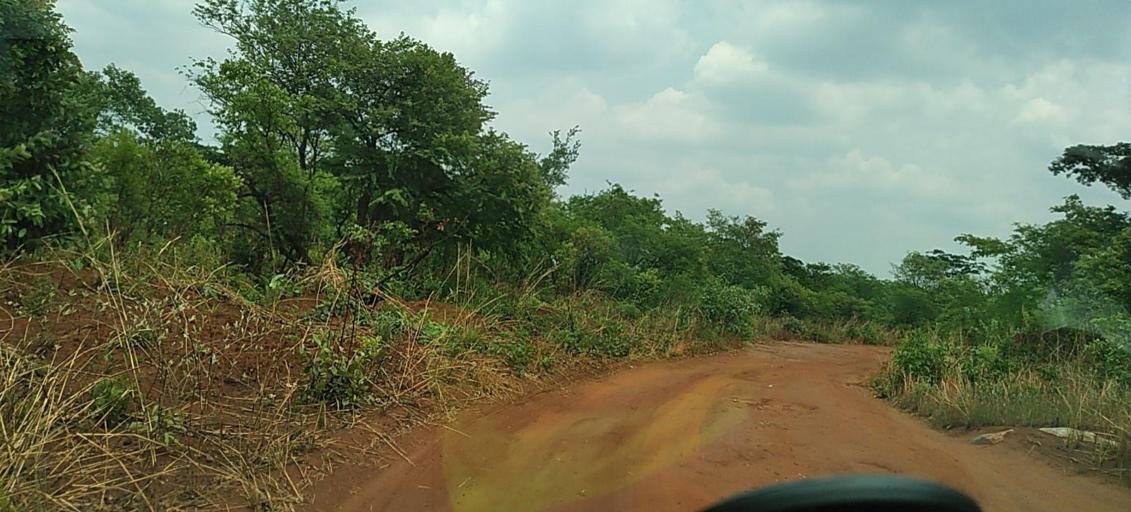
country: ZM
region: North-Western
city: Kansanshi
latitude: -12.0477
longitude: 26.3804
